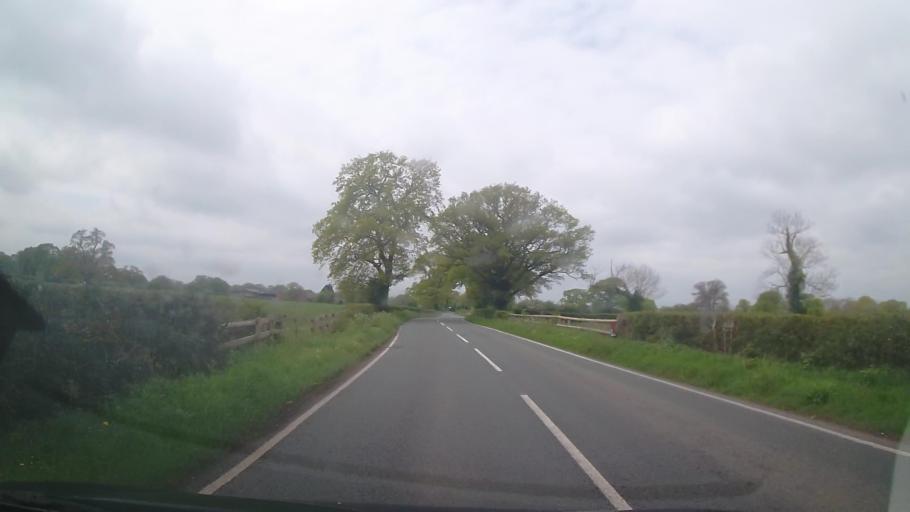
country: GB
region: England
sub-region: Shropshire
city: Ellesmere
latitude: 52.9522
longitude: -2.8399
